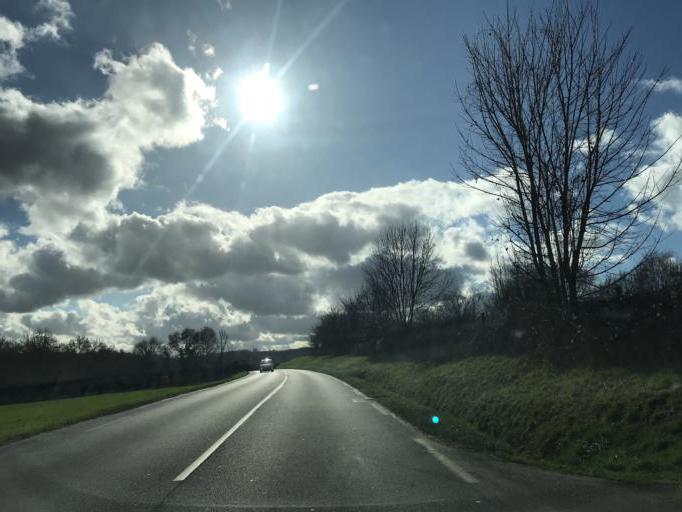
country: FR
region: Rhone-Alpes
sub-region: Departement de l'Ain
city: Sainte-Euphemie
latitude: 45.9775
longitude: 4.7982
